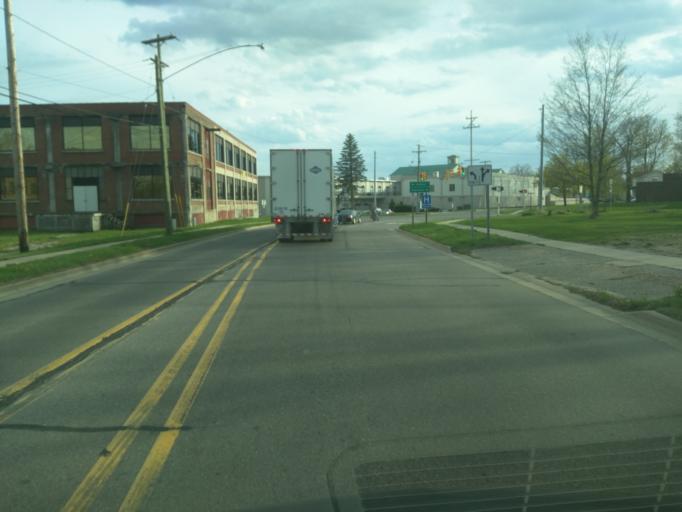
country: US
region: Michigan
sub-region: Eaton County
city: Eaton Rapids
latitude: 42.5154
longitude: -84.6559
